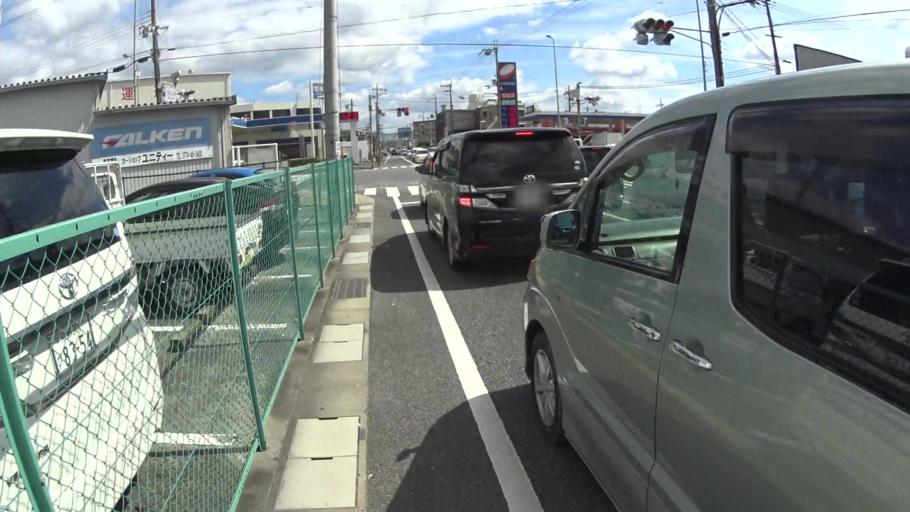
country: JP
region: Kyoto
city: Yawata
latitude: 34.8806
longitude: 135.7363
